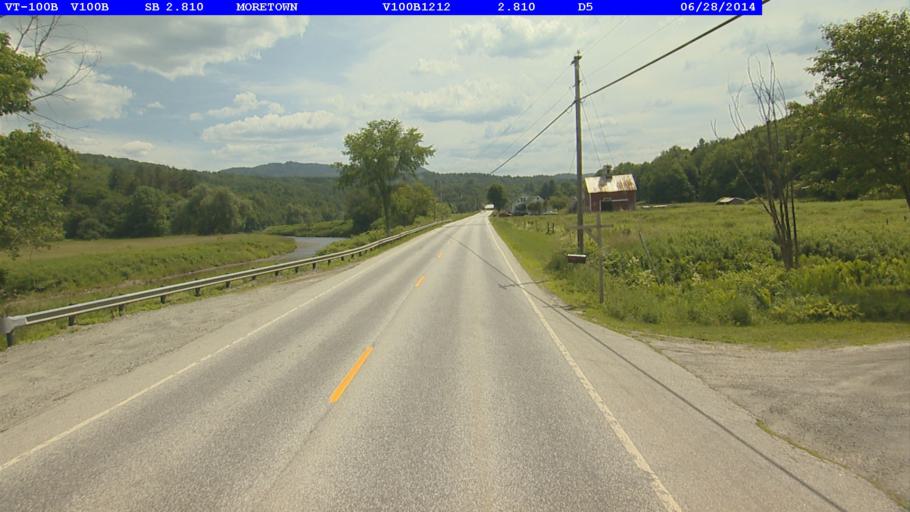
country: US
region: Vermont
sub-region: Washington County
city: Waterbury
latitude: 44.2697
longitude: -72.7462
